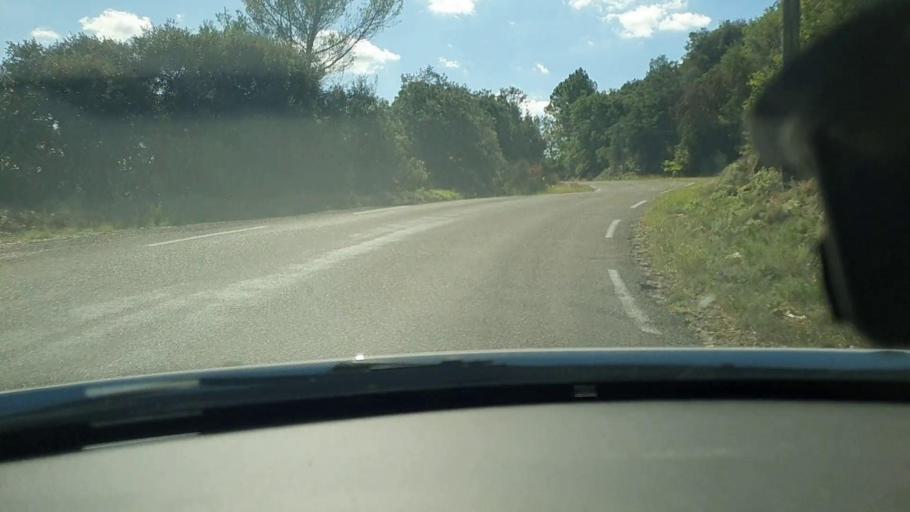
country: FR
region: Languedoc-Roussillon
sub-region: Departement du Gard
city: Goudargues
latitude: 44.1713
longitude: 4.4882
